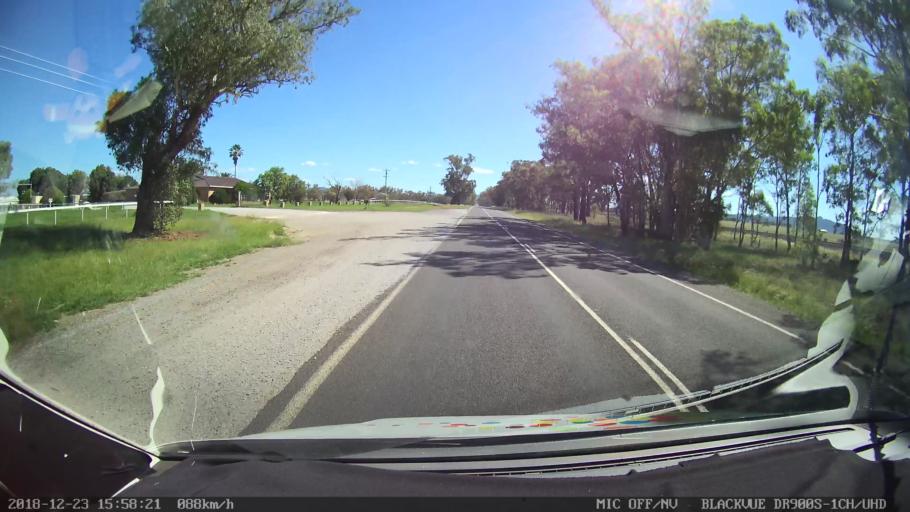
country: AU
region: New South Wales
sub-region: Tamworth Municipality
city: Phillip
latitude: -31.1873
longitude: 150.8424
